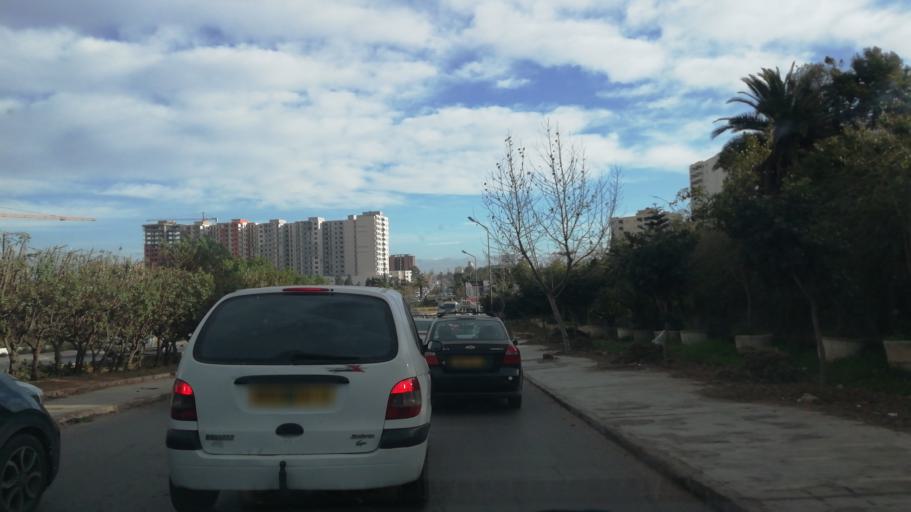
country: DZ
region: Oran
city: Bir el Djir
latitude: 35.7158
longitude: -0.5786
